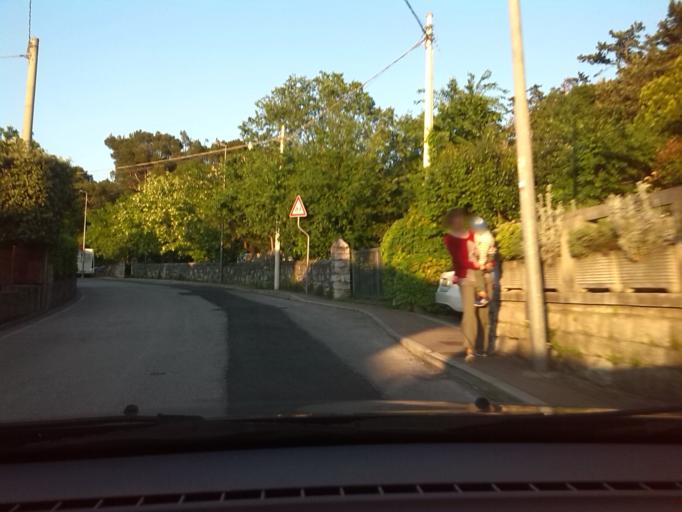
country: IT
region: Friuli Venezia Giulia
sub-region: Provincia di Trieste
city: Duino
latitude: 45.7731
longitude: 13.6070
